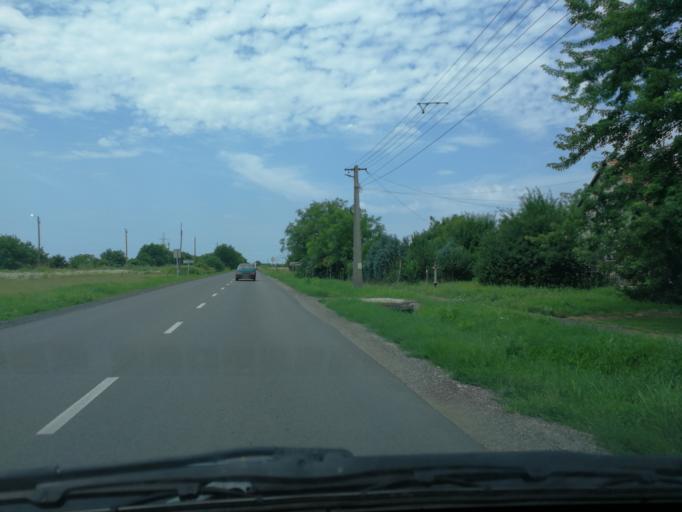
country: HU
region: Baranya
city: Villany
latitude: 45.8484
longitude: 18.3791
